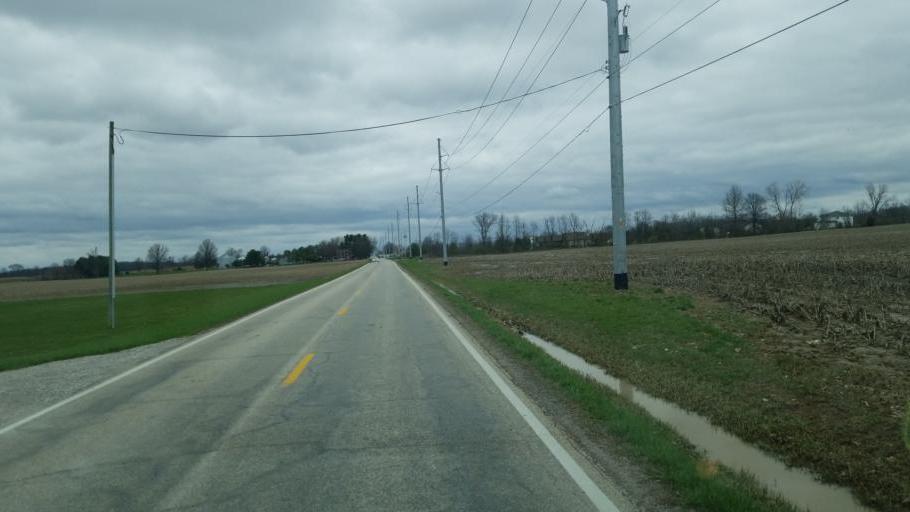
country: US
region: Ohio
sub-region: Delaware County
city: Delaware
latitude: 40.3355
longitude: -83.0996
